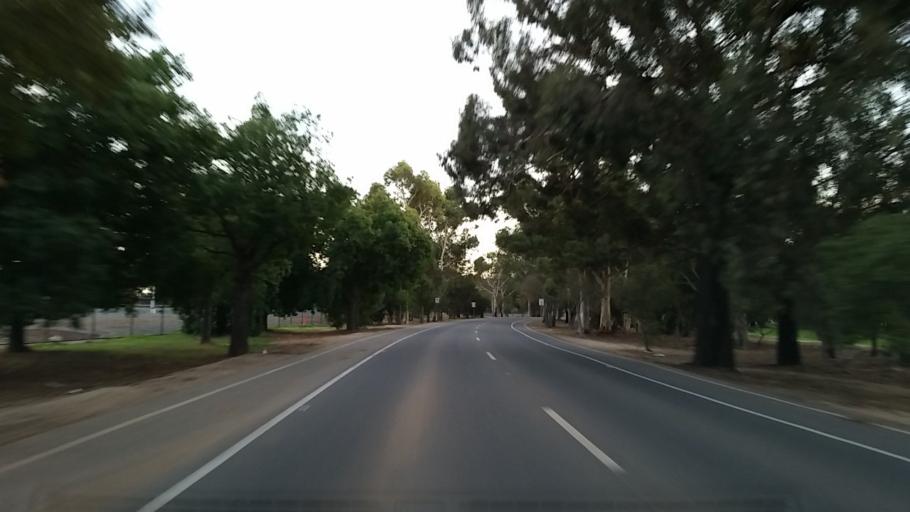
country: AU
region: South Australia
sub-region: Adelaide
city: North Adelaide
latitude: -34.9104
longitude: 138.5816
